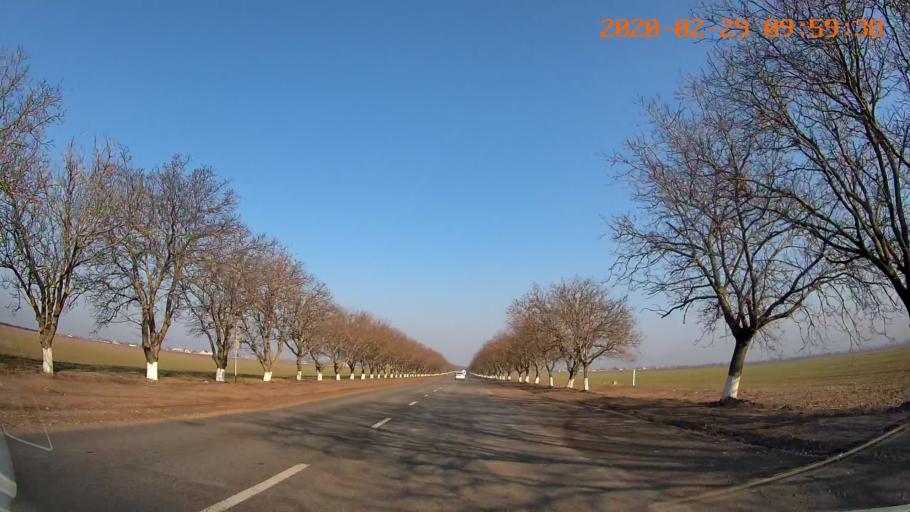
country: MD
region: Telenesti
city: Slobozia
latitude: 46.7590
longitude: 29.6880
